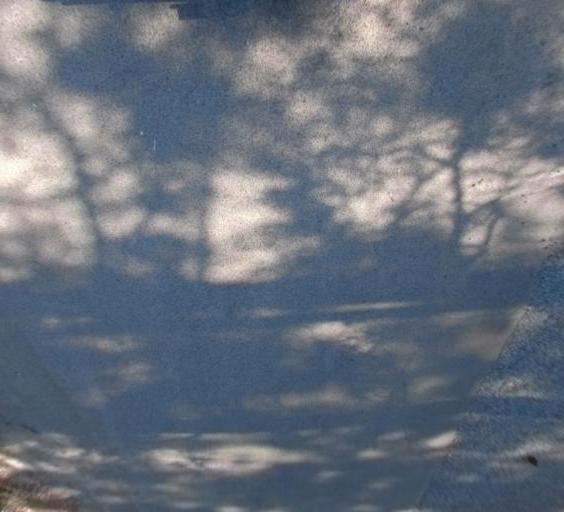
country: US
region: California
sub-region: Madera County
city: Bonadelle Ranchos-Madera Ranchos
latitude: 36.9119
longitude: -119.8022
